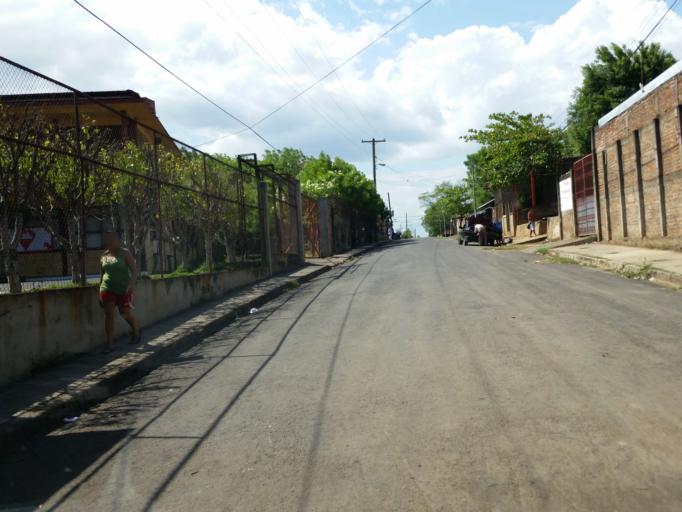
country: NI
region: Leon
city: Leon
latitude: 12.4347
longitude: -86.8988
